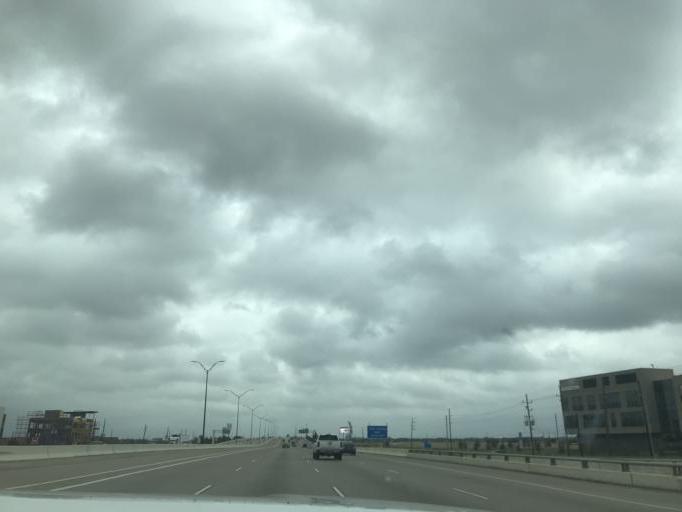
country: US
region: Texas
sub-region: Fort Bend County
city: Greatwood
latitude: 29.5771
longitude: -95.6539
